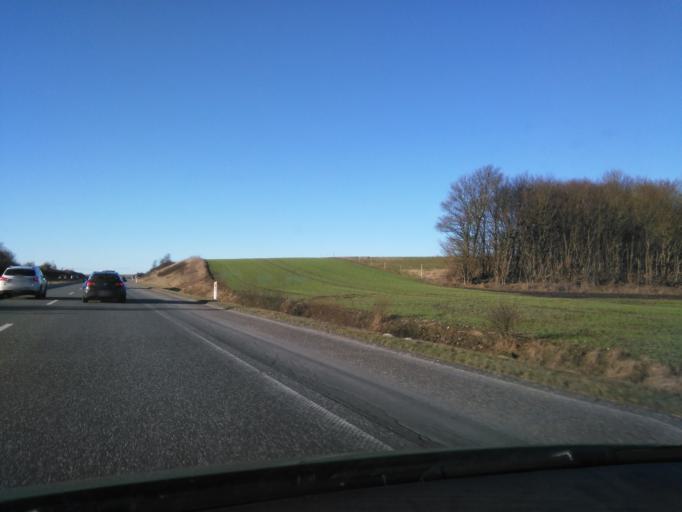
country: DK
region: North Denmark
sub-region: Mariagerfjord Kommune
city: Mariager
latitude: 56.5455
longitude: 9.8899
